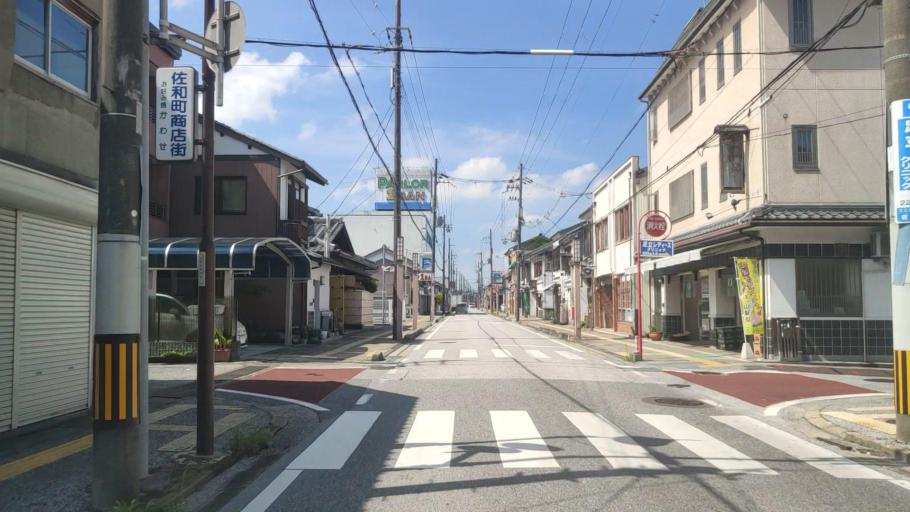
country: JP
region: Shiga Prefecture
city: Hikone
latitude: 35.2719
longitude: 136.2601
